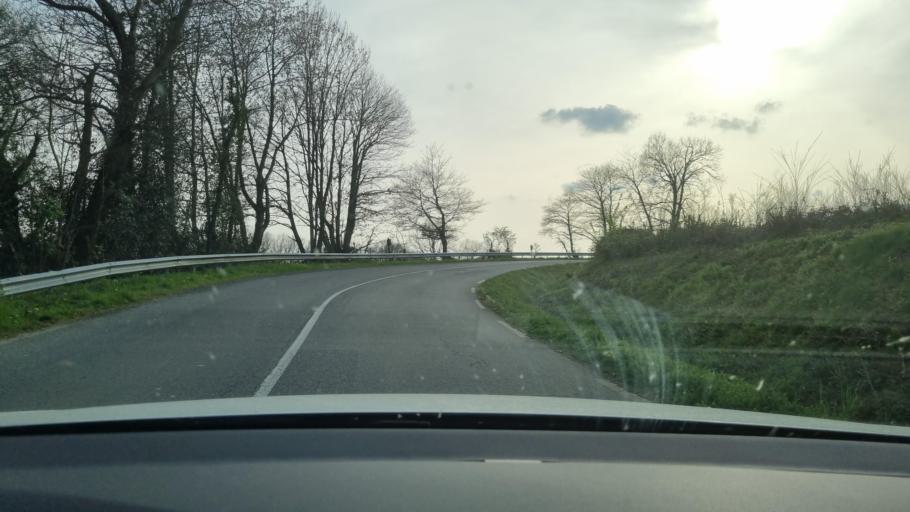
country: FR
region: Aquitaine
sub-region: Departement des Pyrenees-Atlantiques
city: Soumoulou
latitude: 43.3774
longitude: -0.1390
